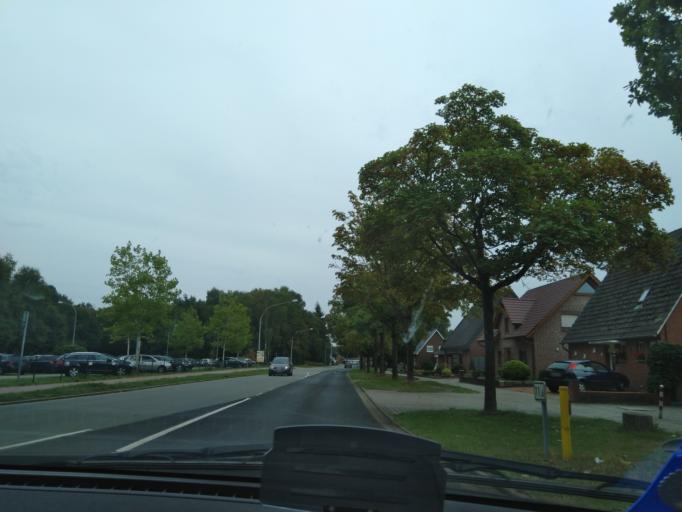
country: DE
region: Lower Saxony
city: Meppen
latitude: 52.6833
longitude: 7.2918
